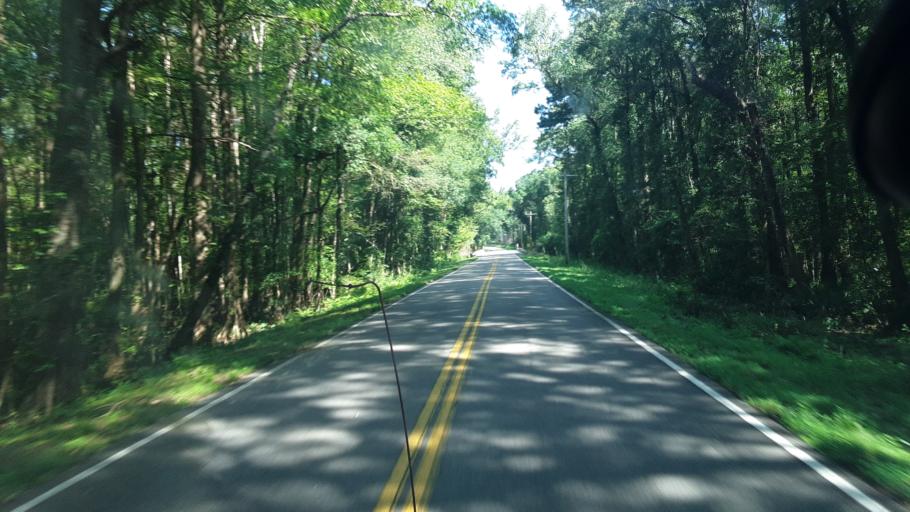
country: US
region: South Carolina
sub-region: Hampton County
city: Varnville
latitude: 32.9068
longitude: -81.0100
